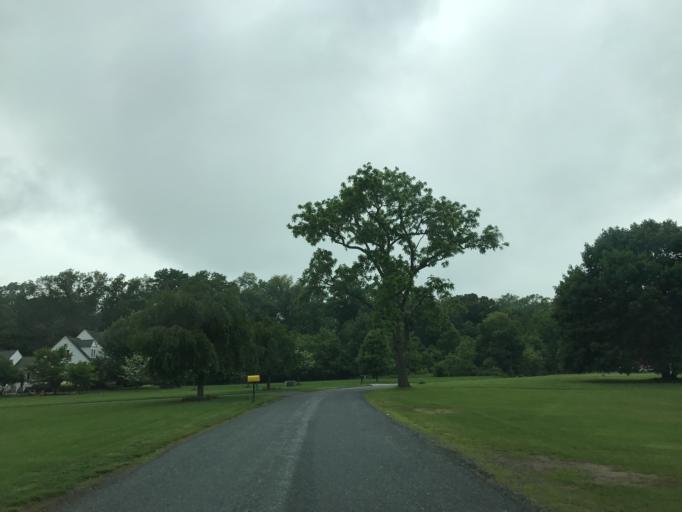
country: US
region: Maryland
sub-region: Harford County
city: Jarrettsville
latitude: 39.7014
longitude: -76.4938
